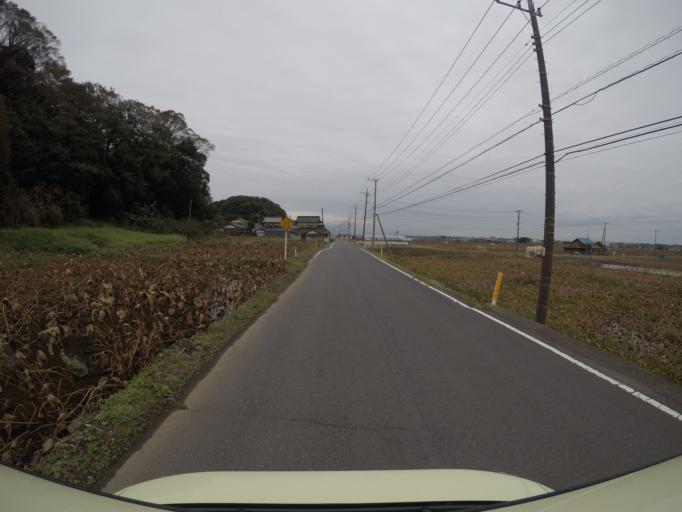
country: JP
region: Ibaraki
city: Ami
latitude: 36.0821
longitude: 140.2437
